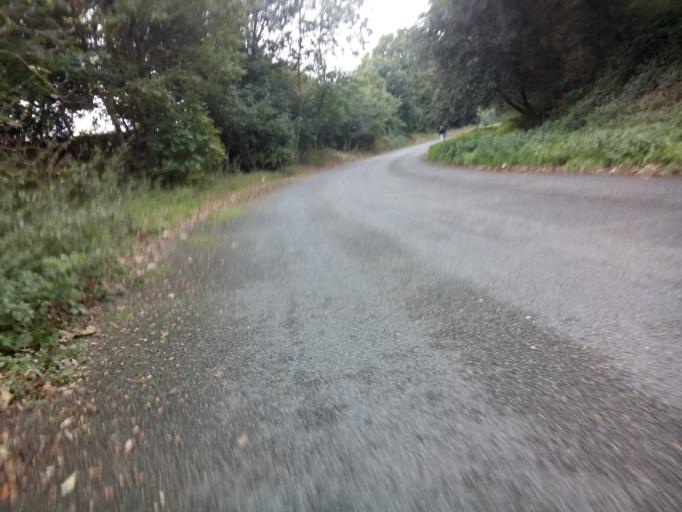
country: GB
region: England
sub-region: Suffolk
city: Ipswich
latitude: 52.0286
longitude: 1.1461
